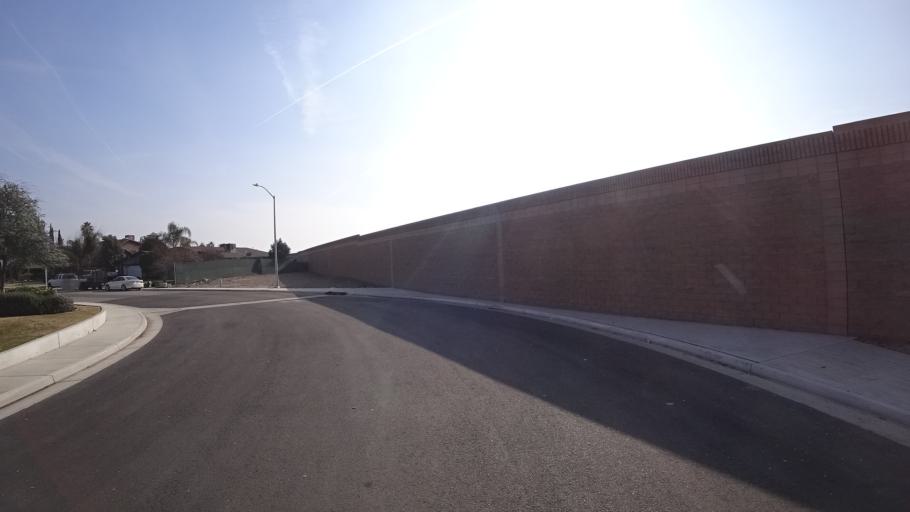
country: US
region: California
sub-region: Kern County
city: Bakersfield
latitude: 35.3620
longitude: -119.0517
